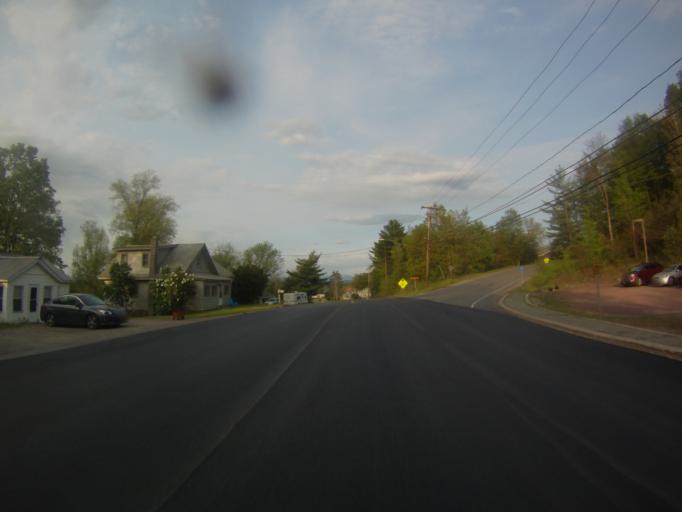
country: US
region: New York
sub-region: Essex County
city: Ticonderoga
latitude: 43.8426
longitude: -73.4523
